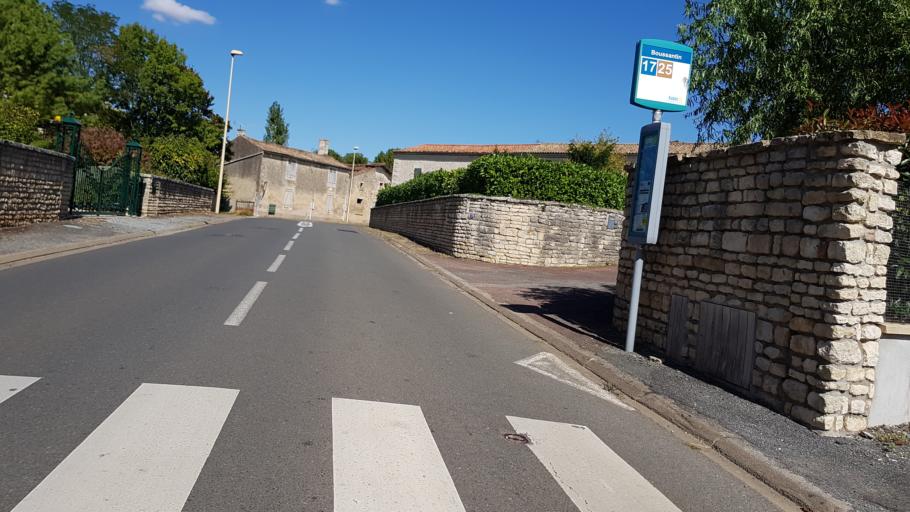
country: FR
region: Poitou-Charentes
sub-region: Departement des Deux-Sevres
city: Vouille
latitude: 46.3128
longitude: -0.3721
